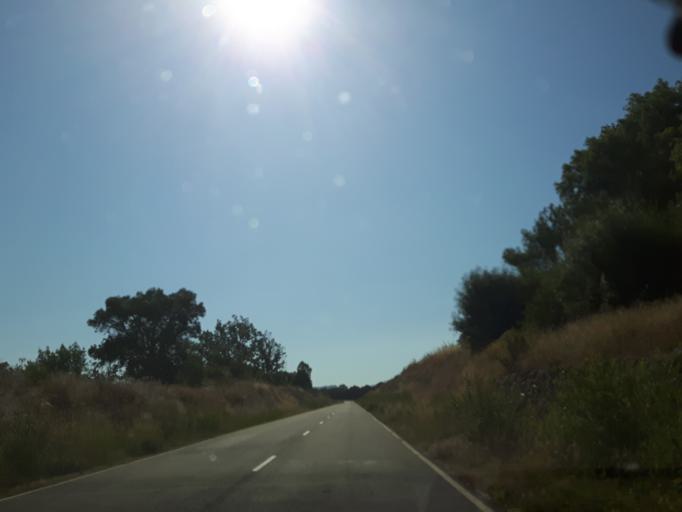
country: ES
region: Castille and Leon
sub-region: Provincia de Salamanca
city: Valdehijaderos
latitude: 40.4208
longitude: -5.8618
